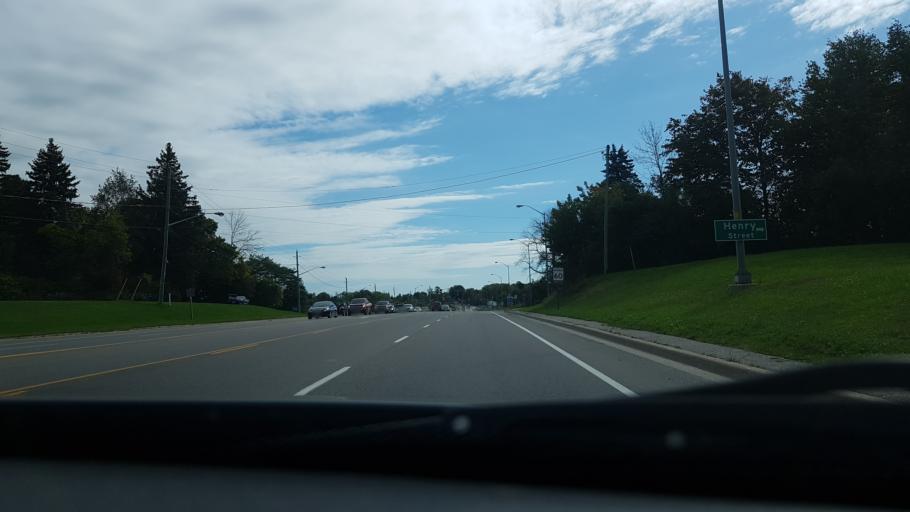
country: CA
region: Ontario
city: Orillia
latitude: 44.6021
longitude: -79.3612
